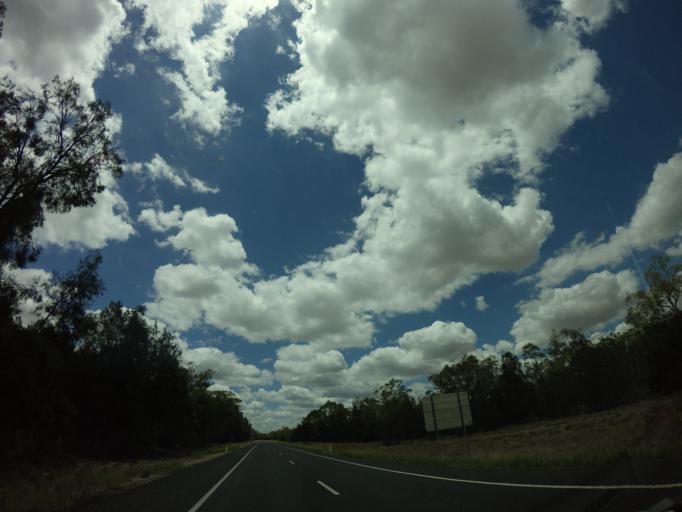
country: AU
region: Queensland
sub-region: Goondiwindi
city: Goondiwindi
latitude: -28.0984
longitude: 150.7254
